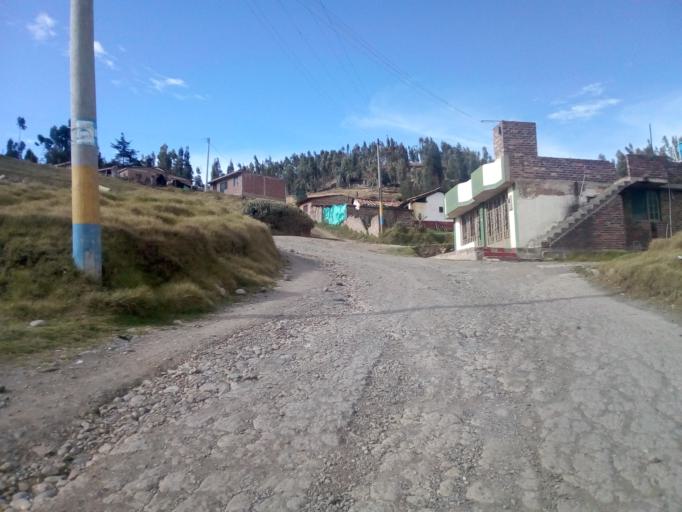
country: CO
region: Boyaca
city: Gameza
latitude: 5.8049
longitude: -72.8061
